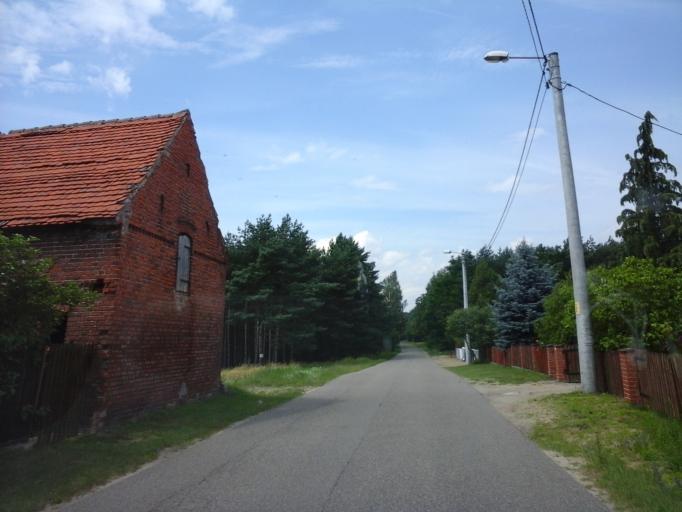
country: PL
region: West Pomeranian Voivodeship
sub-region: Powiat choszczenski
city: Bierzwnik
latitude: 53.0426
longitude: 15.6430
